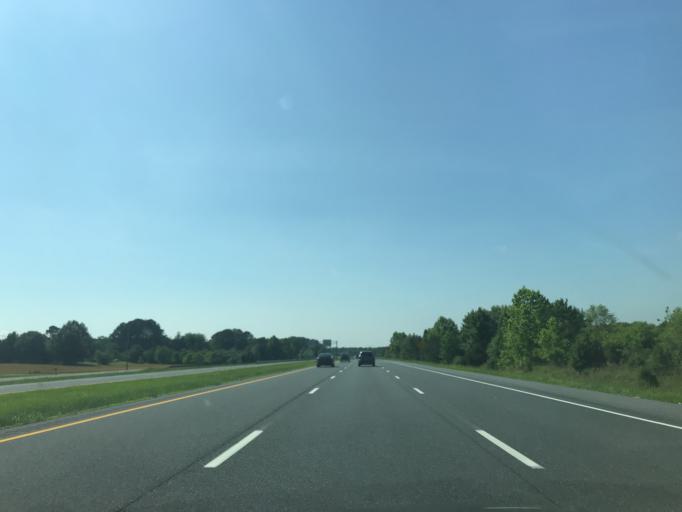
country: US
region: Maryland
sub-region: Wicomico County
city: Hebron
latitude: 38.4059
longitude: -75.6377
